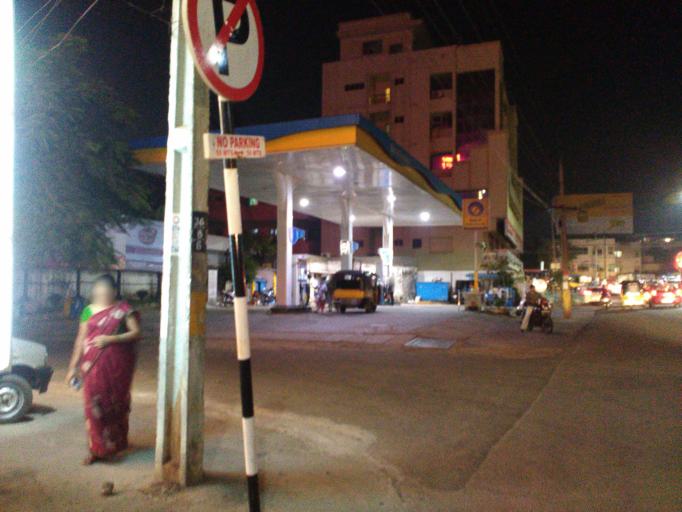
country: IN
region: Andhra Pradesh
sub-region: Vishakhapatnam
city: Yarada
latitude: 17.7427
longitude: 83.3288
